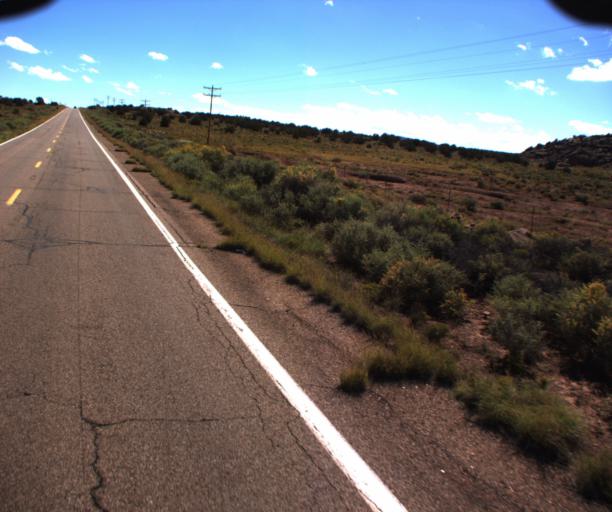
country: US
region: Arizona
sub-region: Apache County
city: Saint Johns
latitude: 34.5446
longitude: -109.6227
